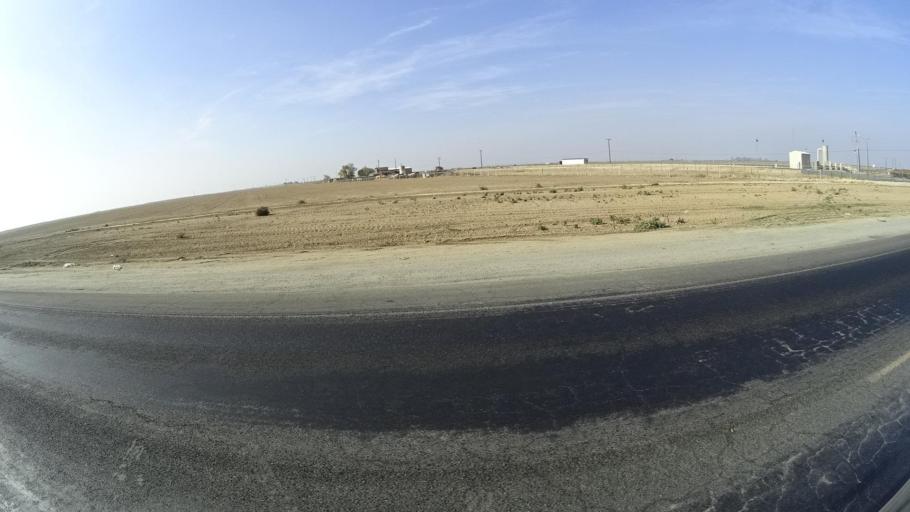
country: US
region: California
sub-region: Kern County
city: McFarland
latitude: 35.7166
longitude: -119.1602
